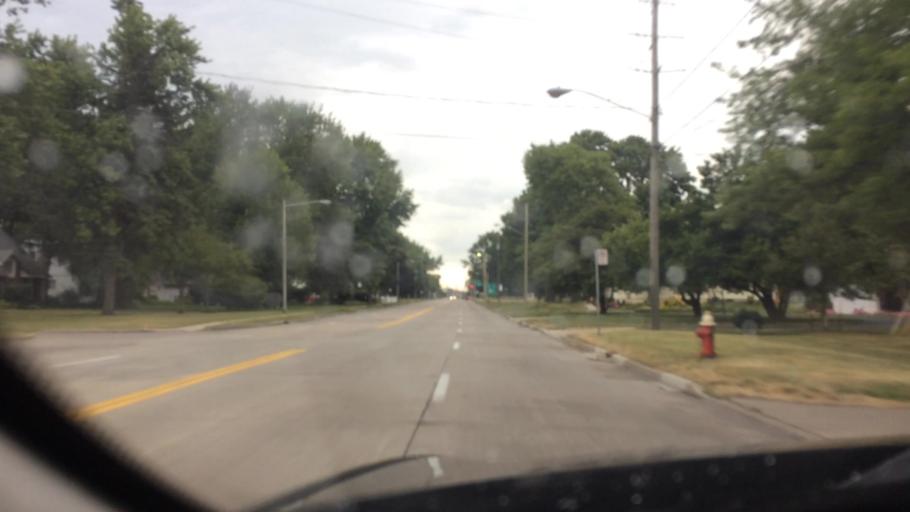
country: US
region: Ohio
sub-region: Lucas County
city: Ottawa Hills
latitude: 41.6839
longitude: -83.6442
